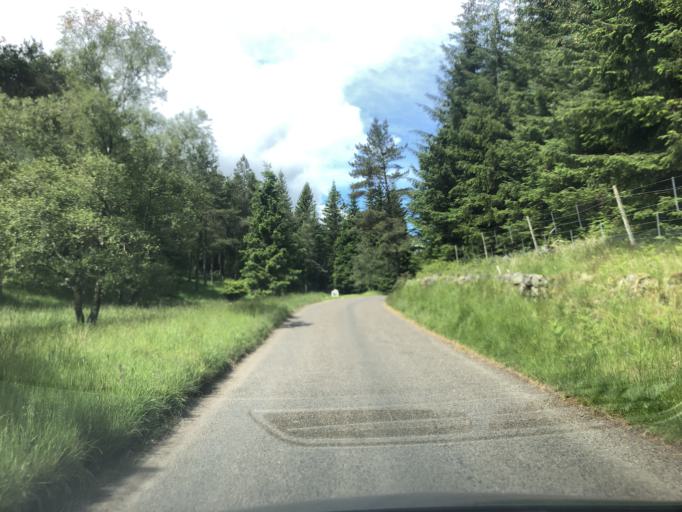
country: GB
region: Scotland
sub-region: Angus
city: Kirriemuir
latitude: 56.8253
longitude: -3.0654
